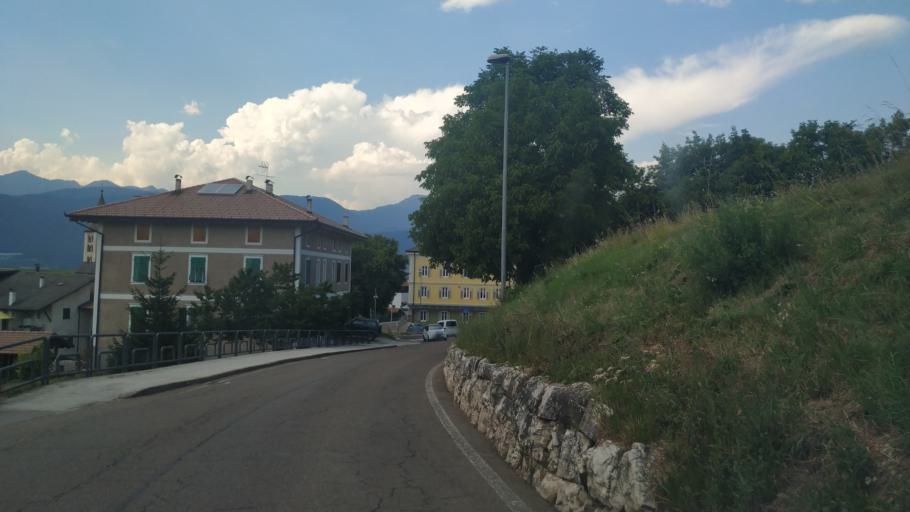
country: IT
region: Trentino-Alto Adige
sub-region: Provincia di Trento
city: Sarnonico
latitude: 46.4176
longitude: 11.1421
